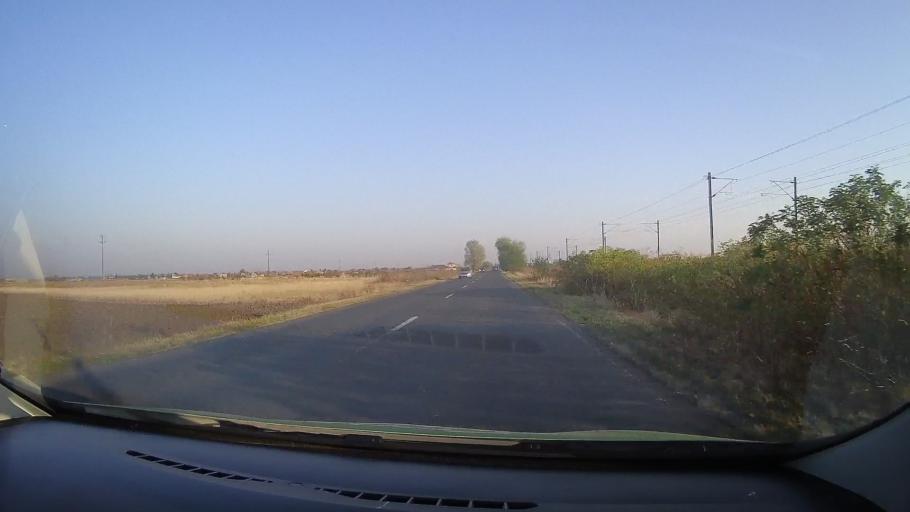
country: RO
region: Arad
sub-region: Comuna Sofronea
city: Sofronea
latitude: 46.2657
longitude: 21.3164
